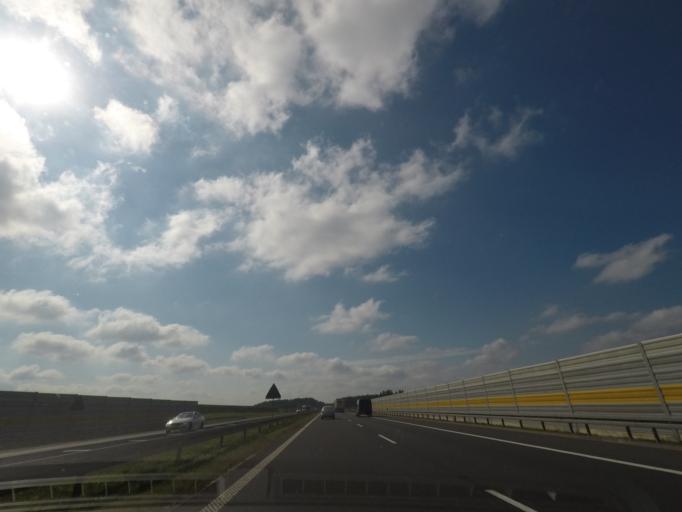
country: PL
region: Pomeranian Voivodeship
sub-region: Powiat starogardzki
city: Smetowo Graniczne
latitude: 53.6820
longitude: 18.6335
